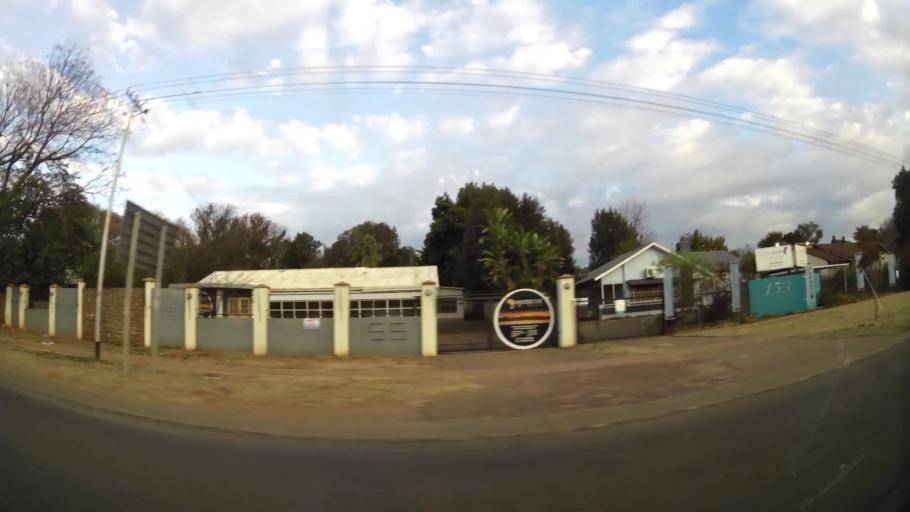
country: ZA
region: Gauteng
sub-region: City of Tshwane Metropolitan Municipality
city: Pretoria
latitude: -25.7419
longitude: 28.3051
